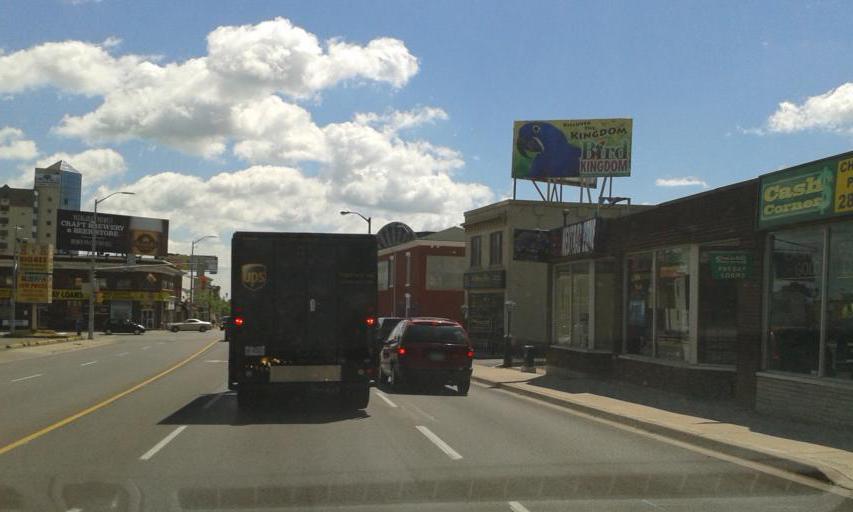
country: CA
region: Ontario
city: Niagara Falls
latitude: 43.0895
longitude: -79.0938
